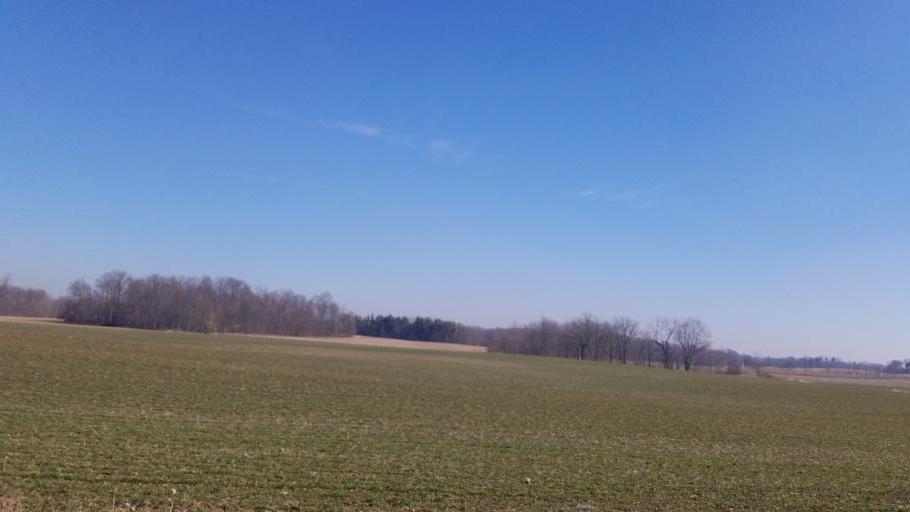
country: US
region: Ohio
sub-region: Richland County
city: Shelby
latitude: 40.8813
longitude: -82.5471
